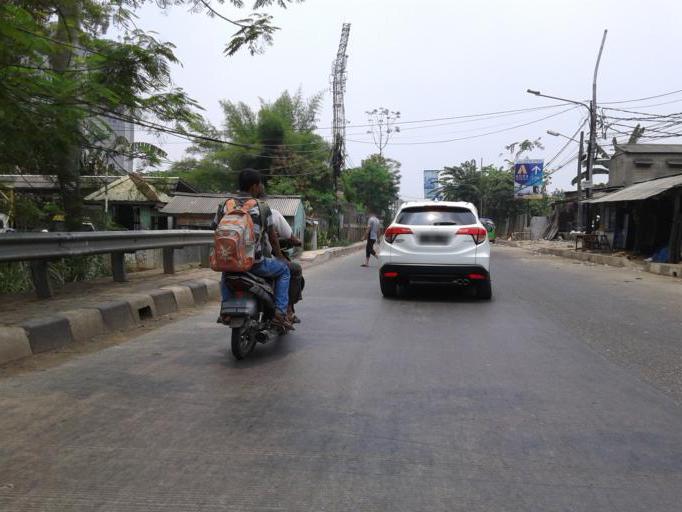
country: ID
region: West Java
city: Pamulang
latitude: -6.3239
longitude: 106.7452
